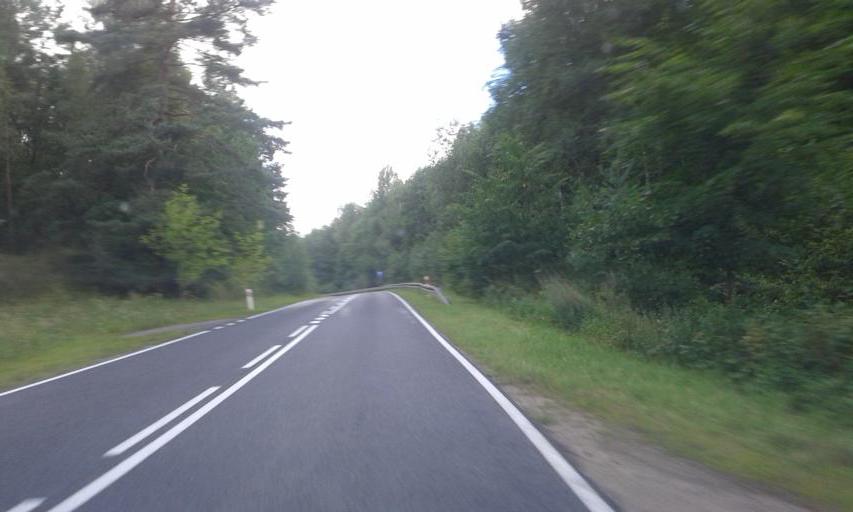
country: PL
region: West Pomeranian Voivodeship
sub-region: Powiat koszalinski
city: Polanow
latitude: 54.0224
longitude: 16.7242
